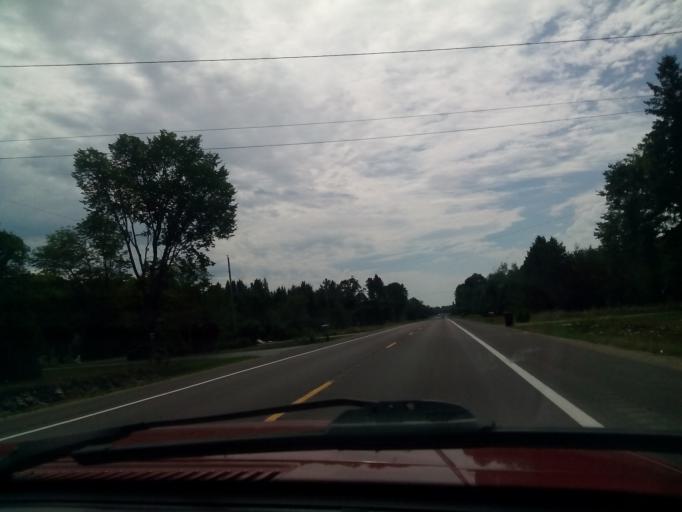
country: US
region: Michigan
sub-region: Schoolcraft County
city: Manistique
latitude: 46.0759
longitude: -85.9583
